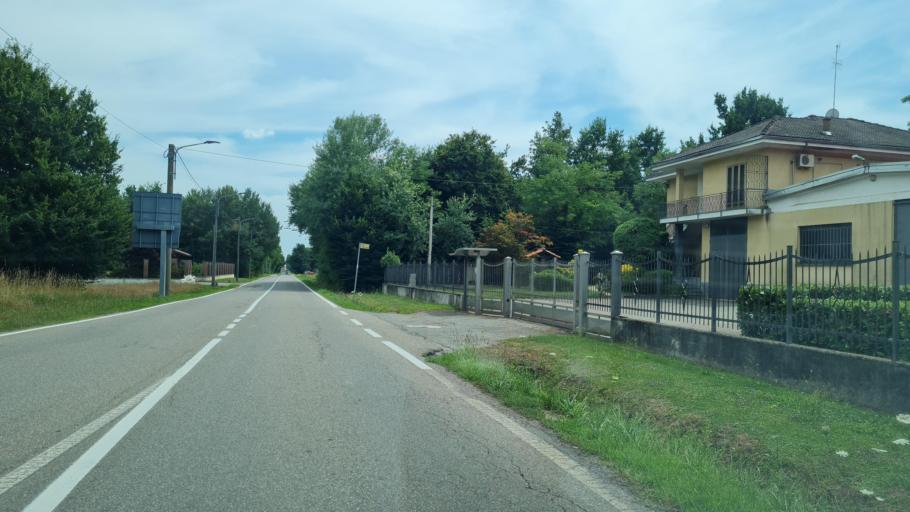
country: IT
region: Piedmont
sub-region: Provincia di Biella
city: Cossato
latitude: 45.5508
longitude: 8.2088
